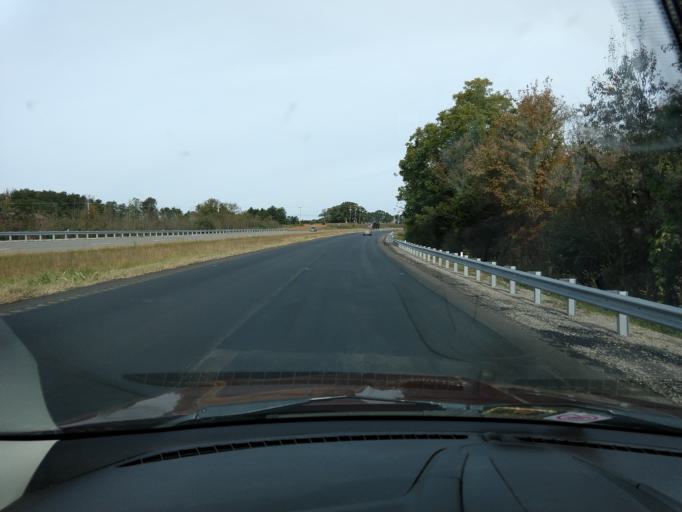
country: US
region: Virginia
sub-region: Pittsylvania County
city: Chatham
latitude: 36.8697
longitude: -79.4081
